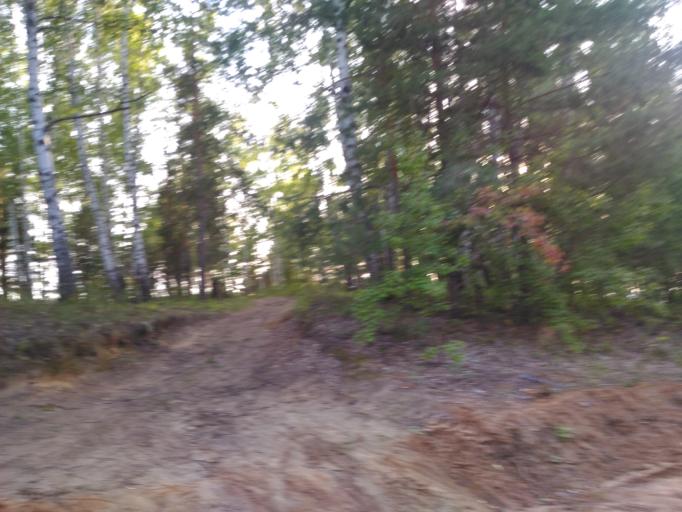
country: RU
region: Ulyanovsk
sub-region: Ulyanovskiy Rayon
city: Ulyanovsk
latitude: 54.3571
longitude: 48.5163
